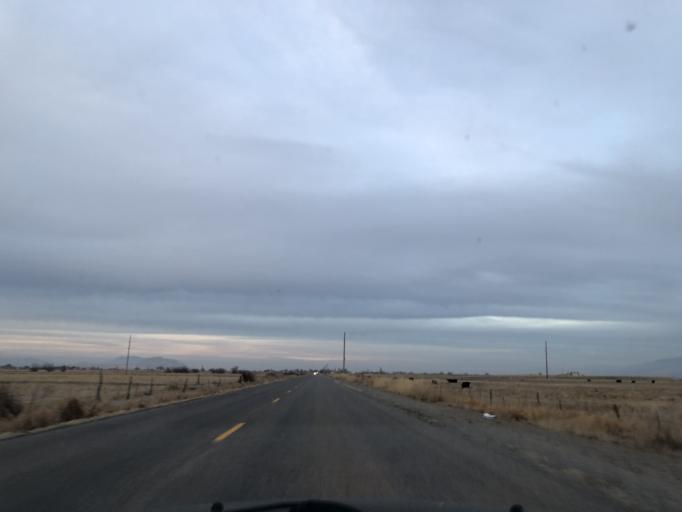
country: US
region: Utah
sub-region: Cache County
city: Benson
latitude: 41.7624
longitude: -111.9117
